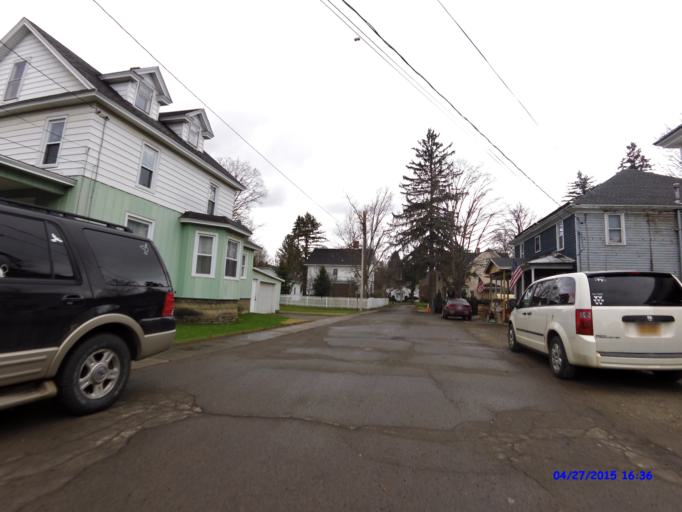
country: US
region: New York
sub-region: Cattaraugus County
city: Franklinville
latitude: 42.3381
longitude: -78.4541
